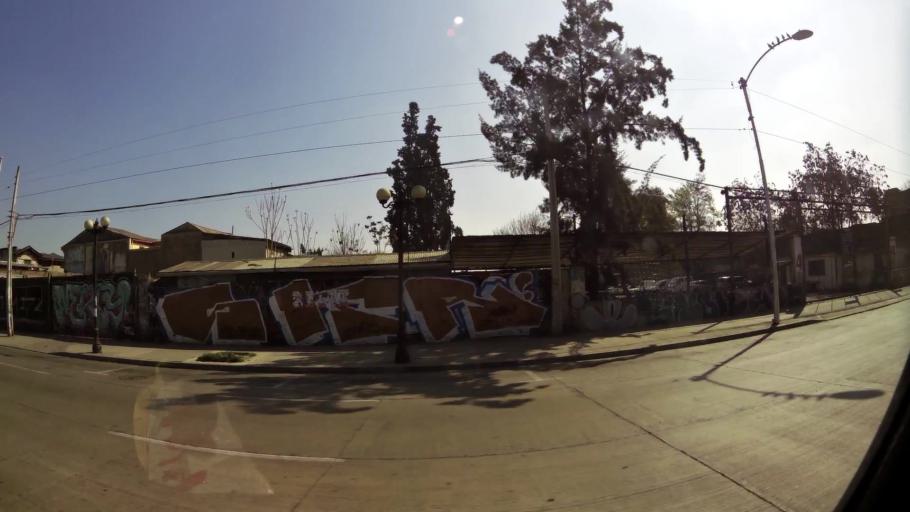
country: CL
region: Santiago Metropolitan
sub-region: Provincia de Santiago
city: Santiago
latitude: -33.4474
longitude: -70.6793
